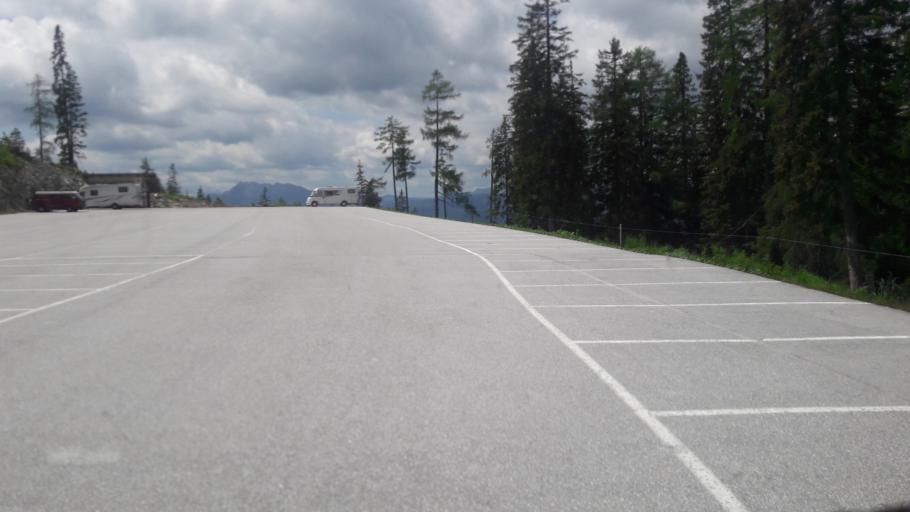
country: AT
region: Styria
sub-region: Politischer Bezirk Liezen
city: Tauplitz
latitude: 47.5919
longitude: 13.9847
